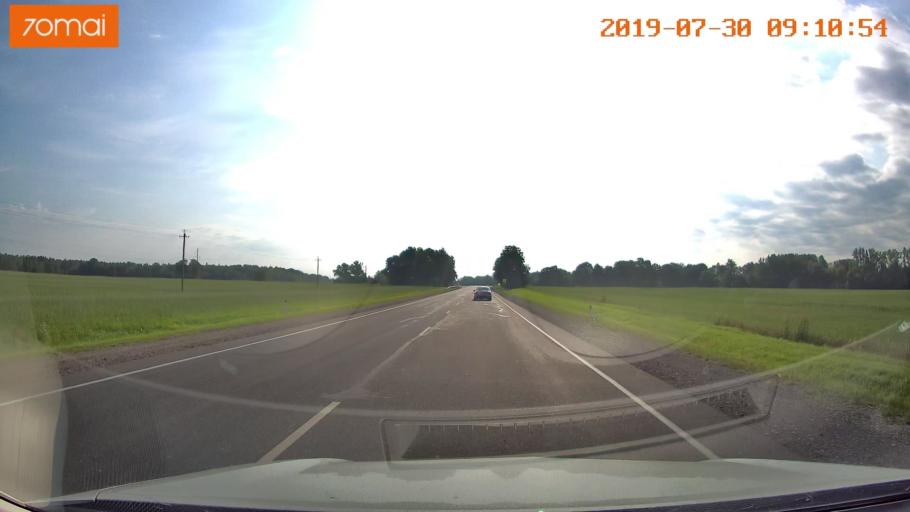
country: RU
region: Kaliningrad
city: Nesterov
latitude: 54.6119
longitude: 22.4384
